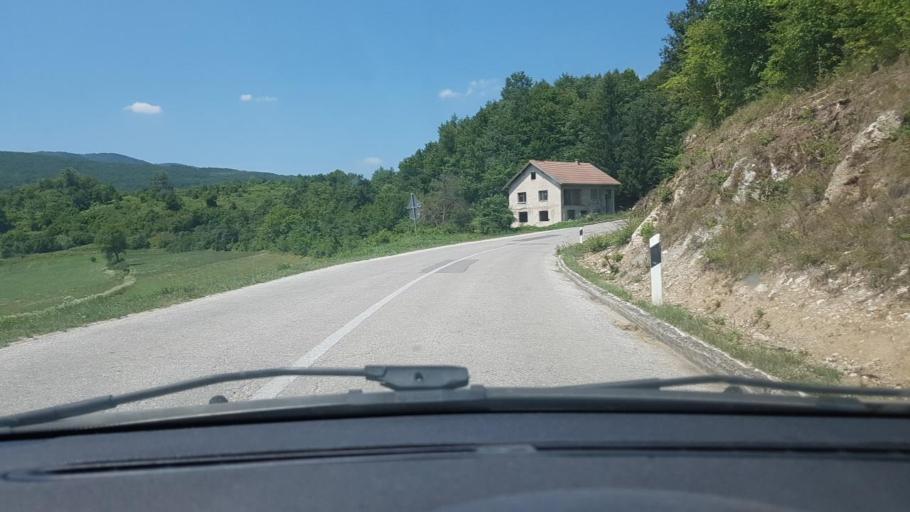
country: BA
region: Federation of Bosnia and Herzegovina
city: Orasac
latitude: 44.5949
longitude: 16.0773
